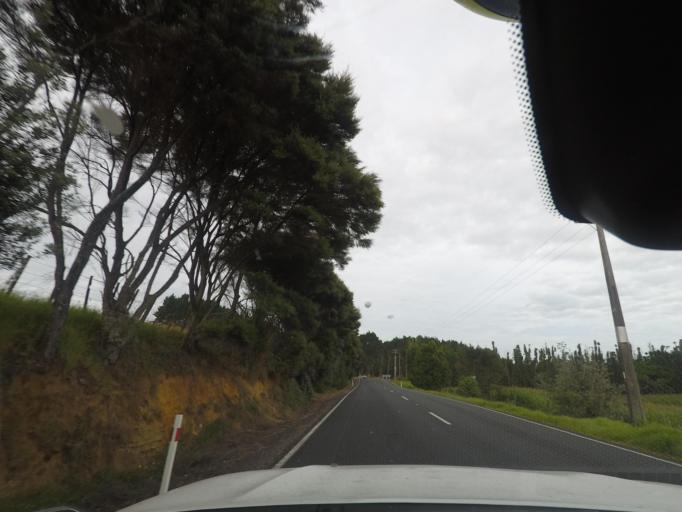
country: NZ
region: Auckland
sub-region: Auckland
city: Parakai
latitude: -36.5178
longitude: 174.2564
